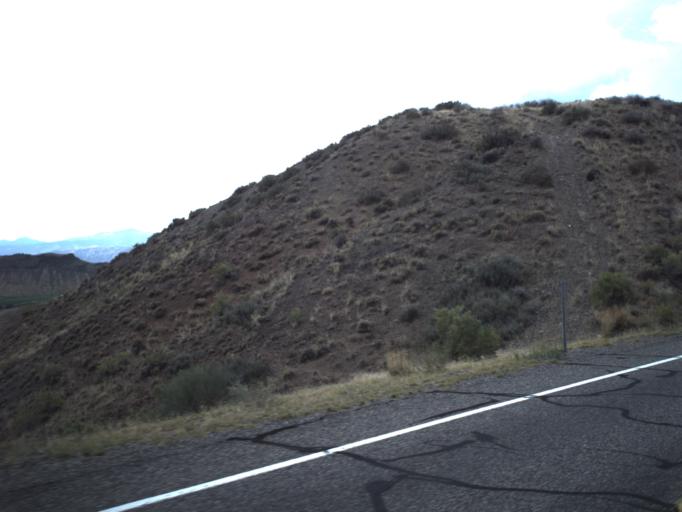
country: US
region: Utah
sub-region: Sevier County
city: Richfield
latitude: 38.7678
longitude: -111.9789
